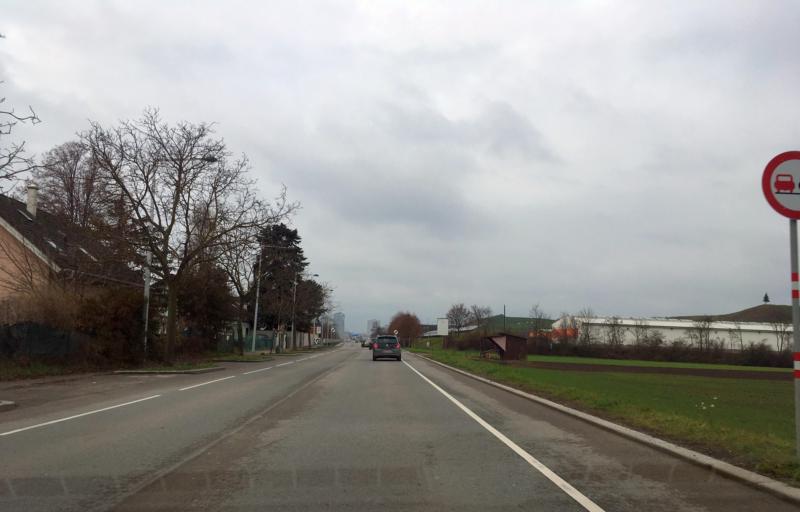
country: AT
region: Lower Austria
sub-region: Politischer Bezirk Wien-Umgebung
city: Gerasdorf bei Wien
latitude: 48.2566
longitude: 16.4878
